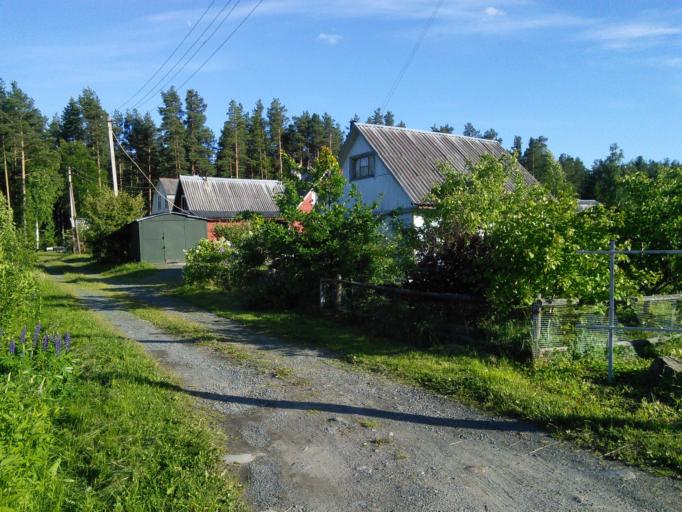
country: RU
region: Republic of Karelia
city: Shuya
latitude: 61.8509
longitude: 34.1453
